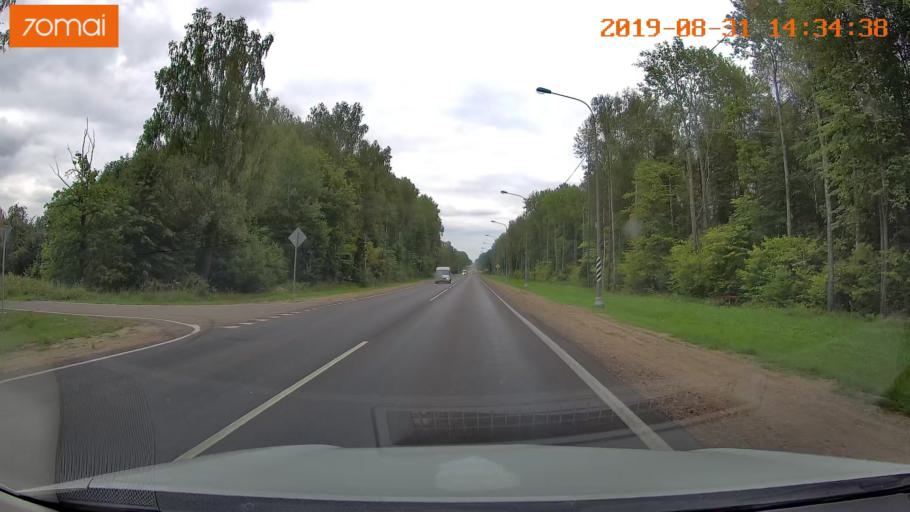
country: RU
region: Smolensk
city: Yekimovichi
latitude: 54.1585
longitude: 33.4412
